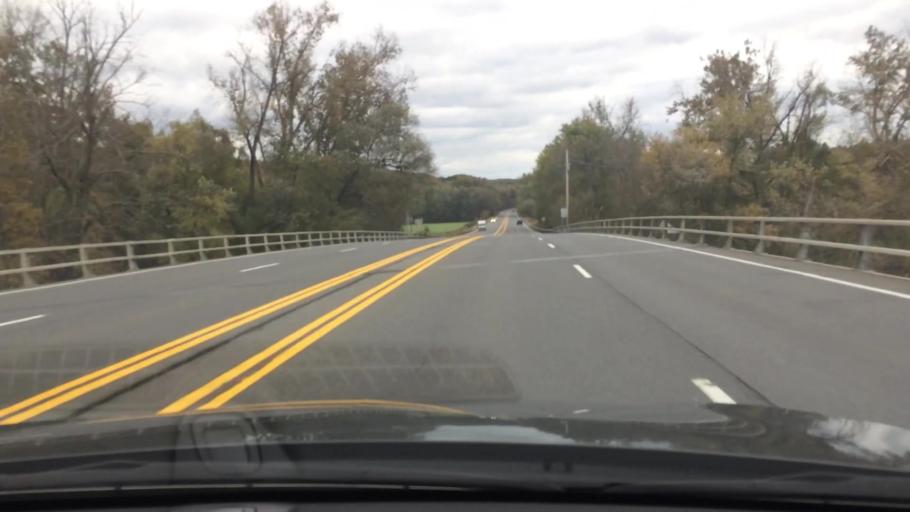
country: US
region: New York
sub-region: Columbia County
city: Kinderhook
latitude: 42.4076
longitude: -73.6907
